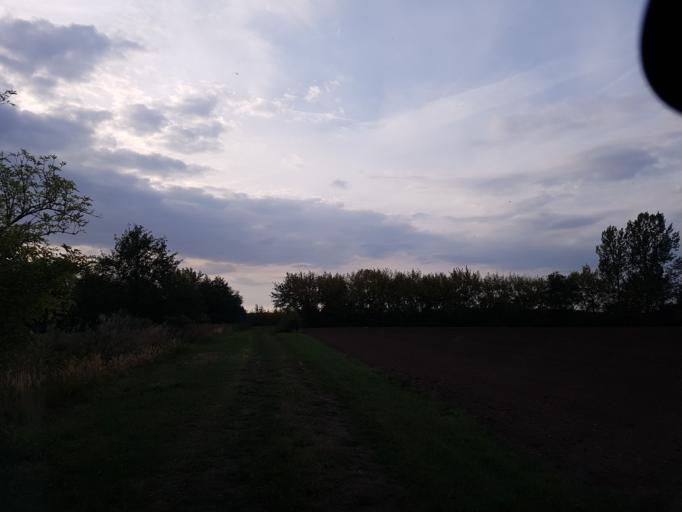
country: DE
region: Brandenburg
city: Bad Liebenwerda
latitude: 51.5495
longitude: 13.4035
